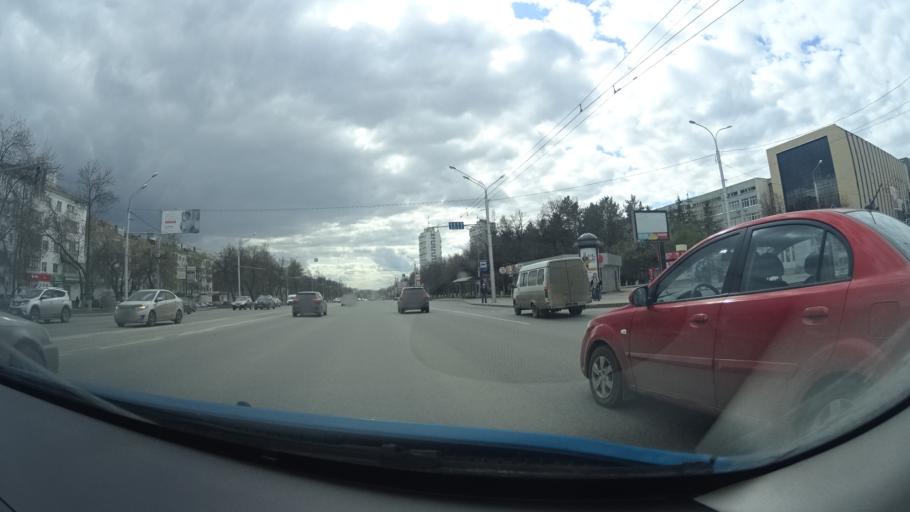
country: RU
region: Bashkortostan
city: Ufa
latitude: 54.7666
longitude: 56.0186
